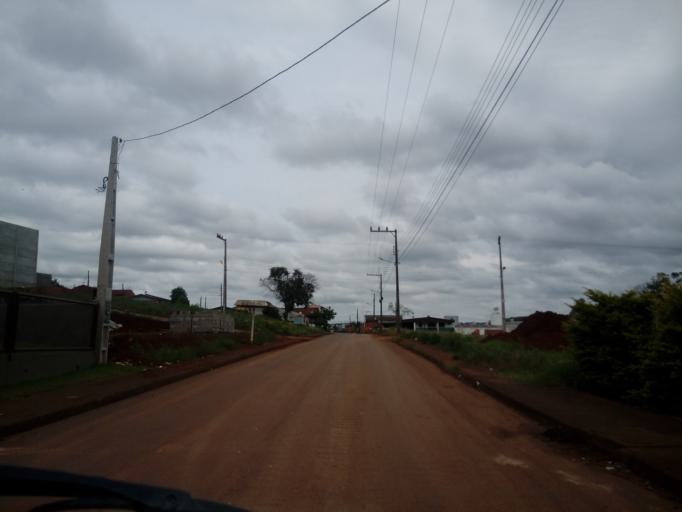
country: BR
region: Santa Catarina
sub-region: Chapeco
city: Chapeco
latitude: -27.0689
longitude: -52.6195
